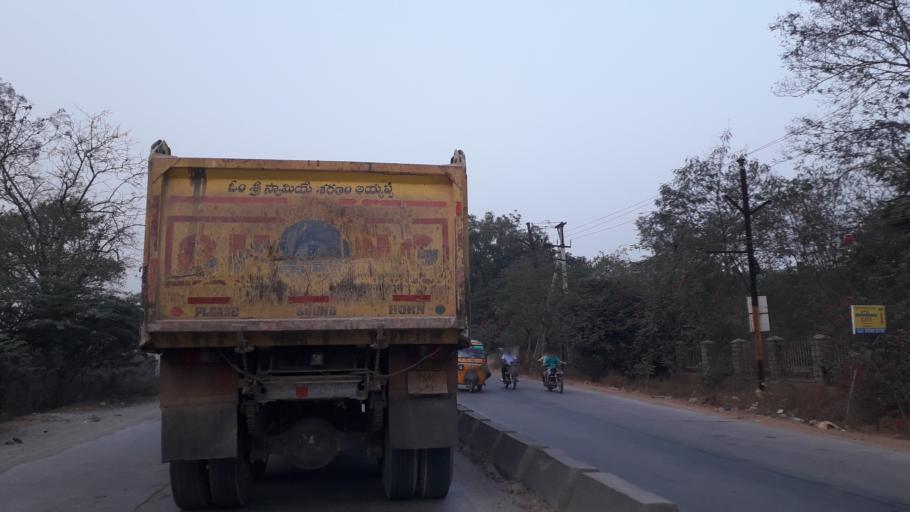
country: IN
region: Telangana
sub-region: Medak
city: Patancheru
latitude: 17.5284
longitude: 78.2535
